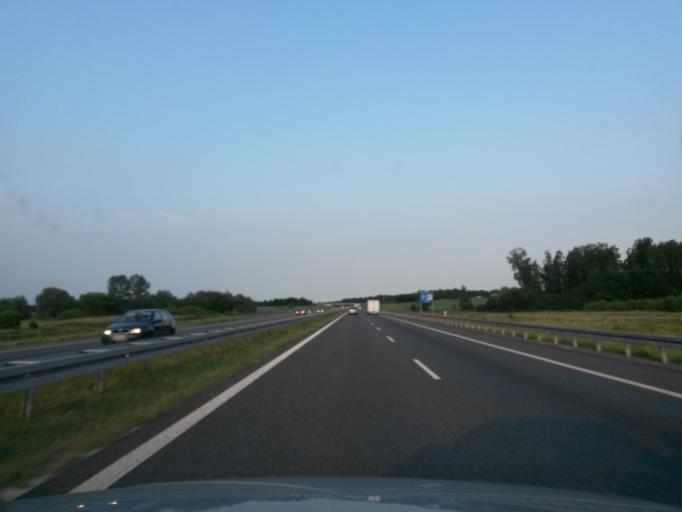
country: PL
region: Lower Silesian Voivodeship
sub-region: Powiat olesnicki
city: Sycow
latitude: 51.2945
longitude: 17.6975
